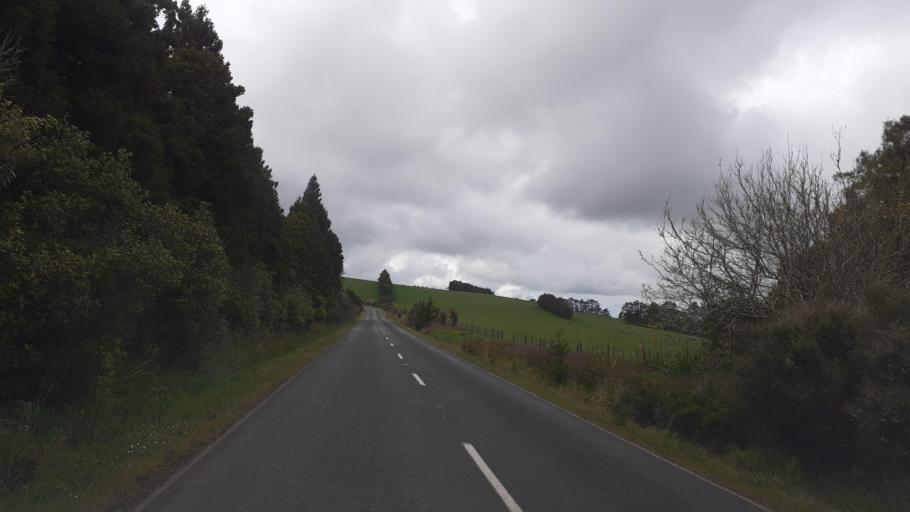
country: NZ
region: Northland
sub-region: Far North District
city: Waimate North
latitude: -35.2619
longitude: 173.8092
